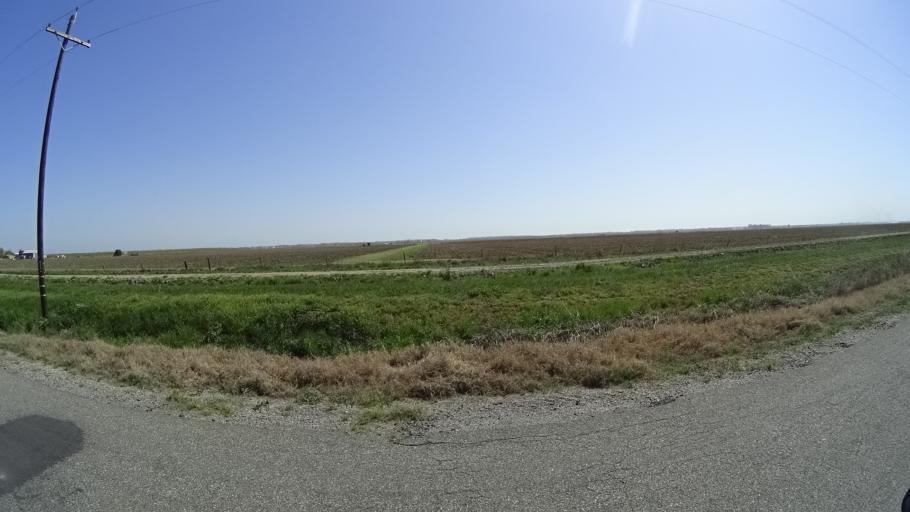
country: US
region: California
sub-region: Glenn County
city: Willows
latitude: 39.5109
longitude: -122.0653
